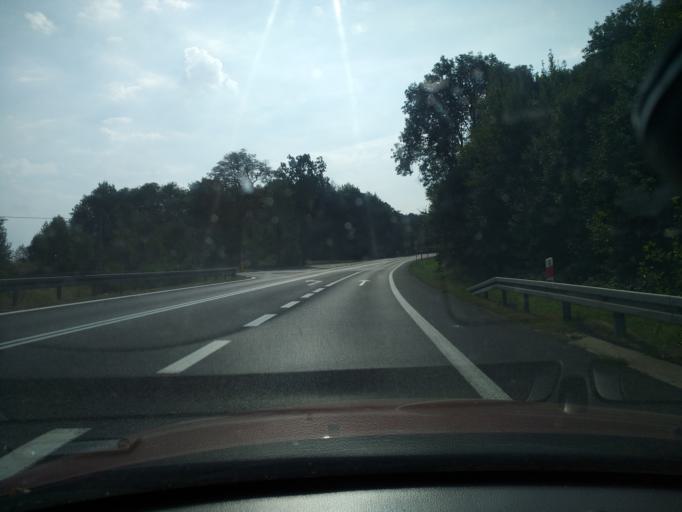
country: PL
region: Lower Silesian Voivodeship
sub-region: Powiat lwowecki
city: Lubomierz
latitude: 50.9986
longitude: 15.4732
